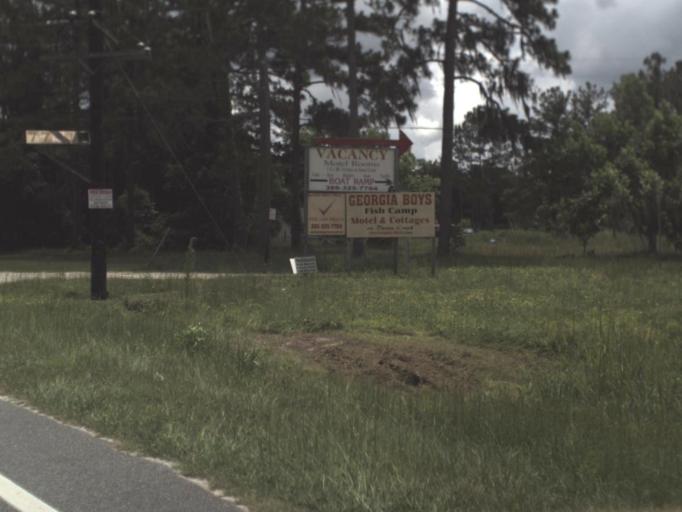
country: US
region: Florida
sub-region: Putnam County
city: Palatka
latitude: 29.5809
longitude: -81.6192
